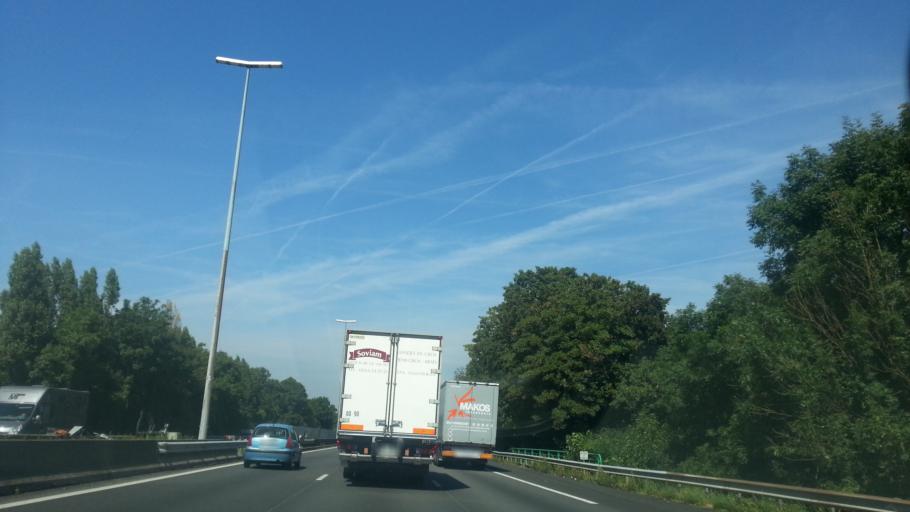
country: FR
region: Ile-de-France
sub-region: Departement du Val-d'Oise
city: Survilliers
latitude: 49.0953
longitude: 2.5504
